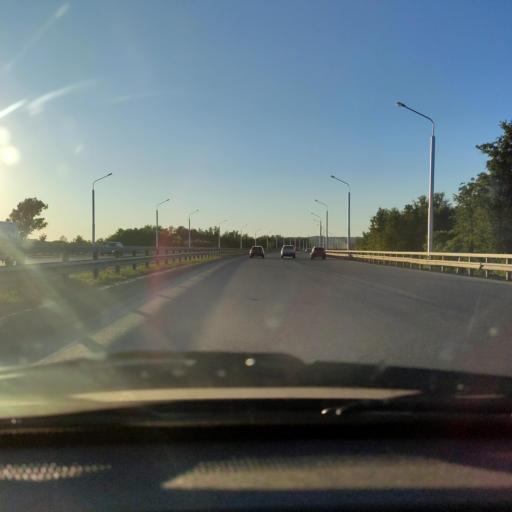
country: RU
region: Bashkortostan
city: Mikhaylovka
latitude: 54.7840
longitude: 55.9124
